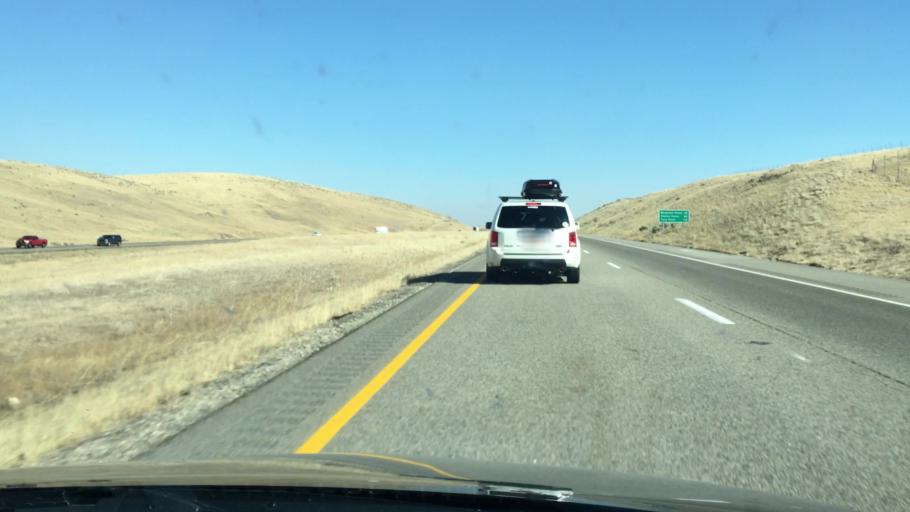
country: US
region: Idaho
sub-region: Ada County
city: Boise
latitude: 43.4988
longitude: -116.1346
